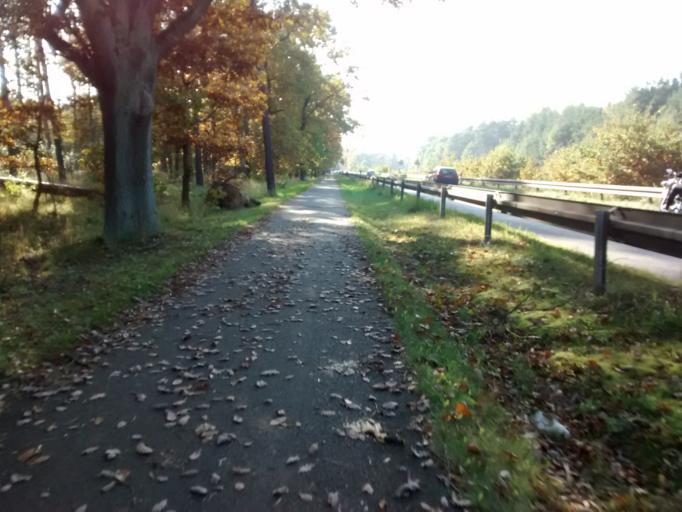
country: DE
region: Brandenburg
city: Hennigsdorf
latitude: 52.6449
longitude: 13.2298
